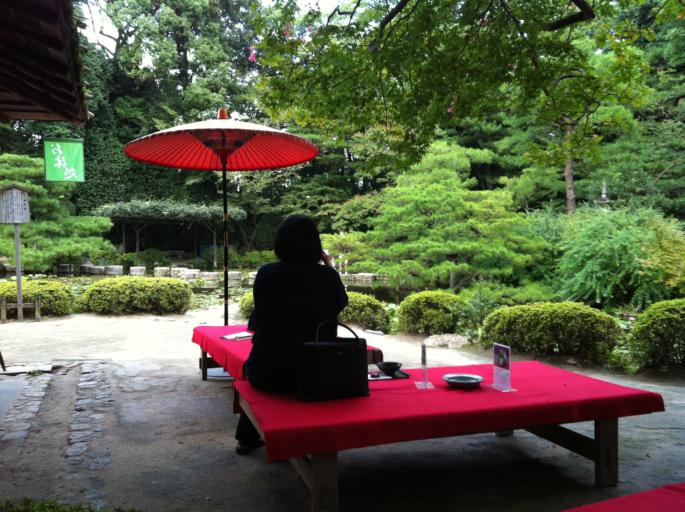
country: JP
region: Kyoto
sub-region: Kyoto-shi
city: Kamigyo-ku
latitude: 35.0168
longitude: 135.7832
